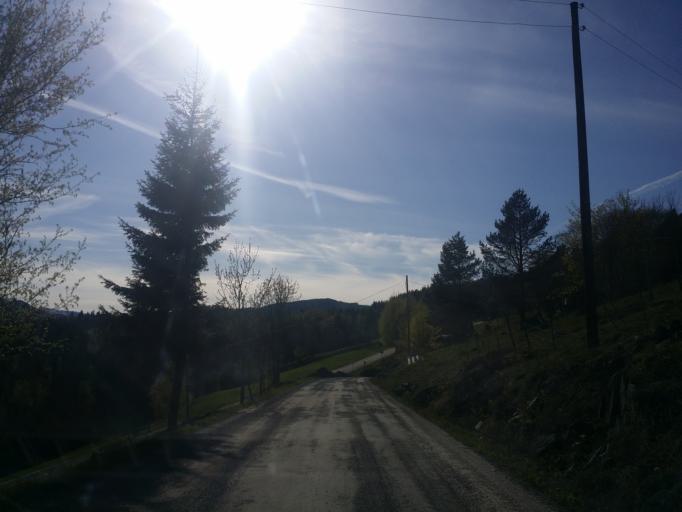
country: NO
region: Telemark
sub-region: Seljord
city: Seljord
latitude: 59.6095
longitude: 8.6828
